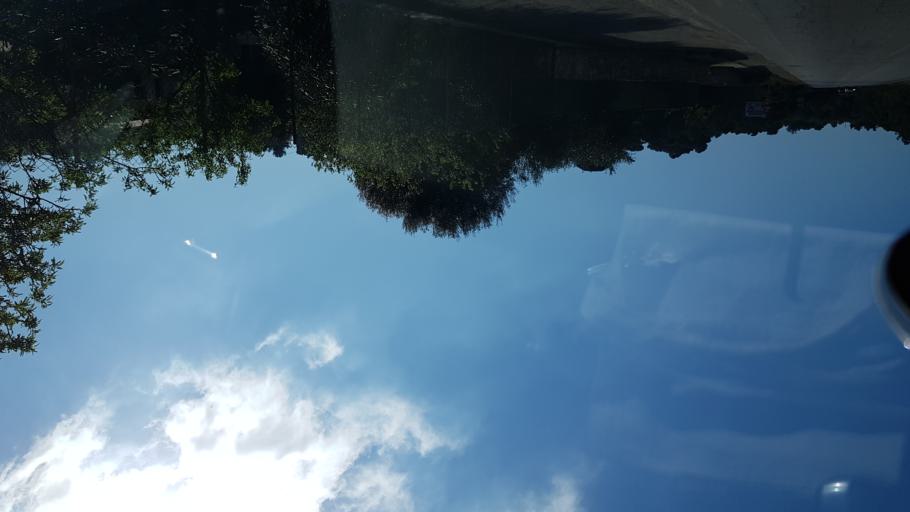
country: IT
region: Apulia
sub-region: Provincia di Brindisi
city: Ostuni
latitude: 40.7296
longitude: 17.5900
